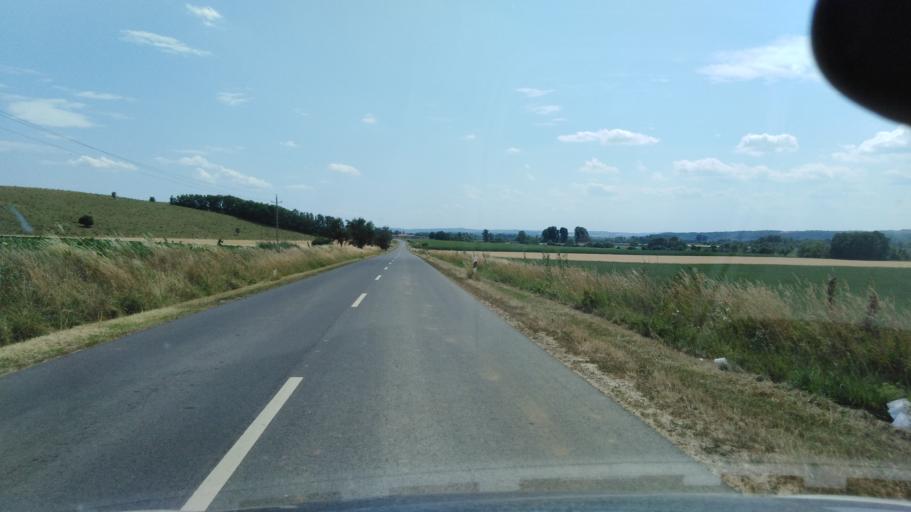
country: HU
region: Nograd
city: Szecseny
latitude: 48.1636
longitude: 19.5365
